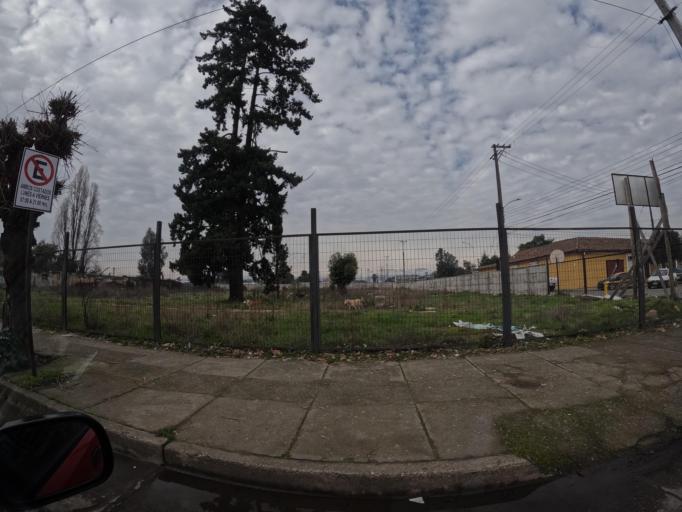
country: CL
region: Maule
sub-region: Provincia de Linares
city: Linares
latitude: -35.8534
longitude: -71.5938
